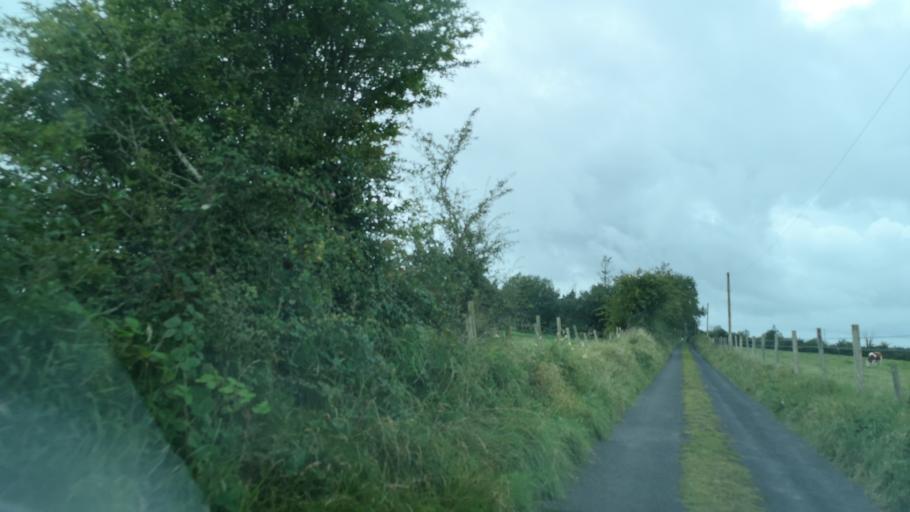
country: IE
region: Connaught
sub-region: County Galway
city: Loughrea
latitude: 53.2962
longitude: -8.6261
